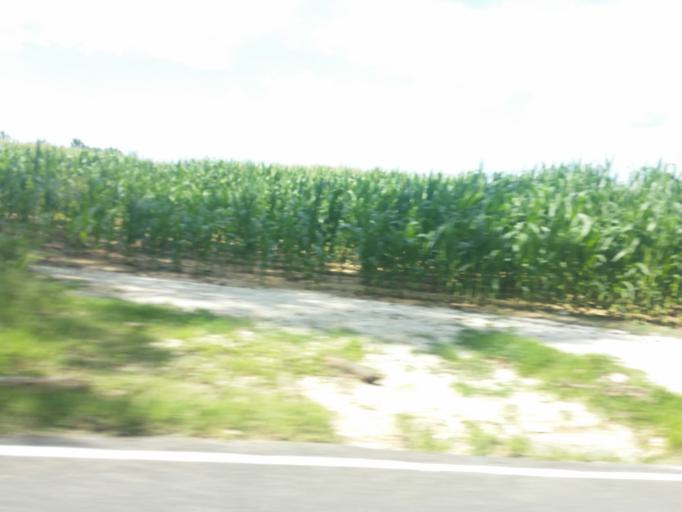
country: US
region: Tennessee
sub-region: Gibson County
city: Milan
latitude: 35.9762
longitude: -88.7902
